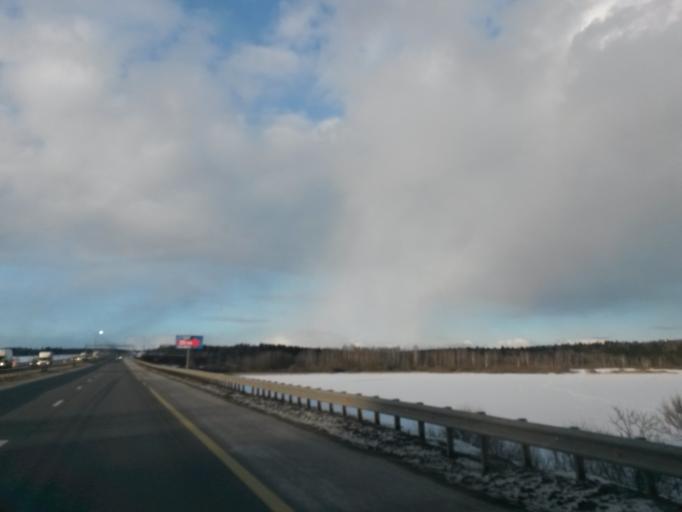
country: RU
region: Moskovskaya
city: Svatkovo
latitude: 56.3300
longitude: 38.2560
